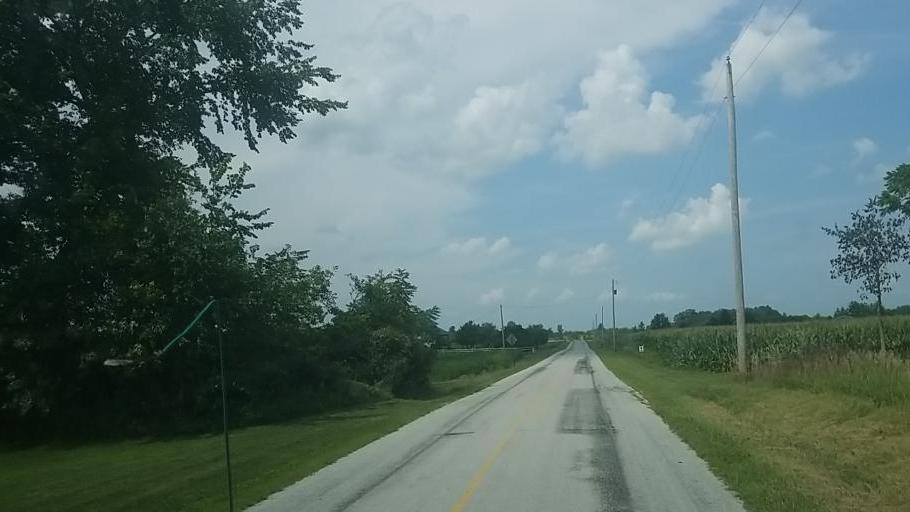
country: US
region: Ohio
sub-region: Hardin County
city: Kenton
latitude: 40.7492
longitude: -83.6024
